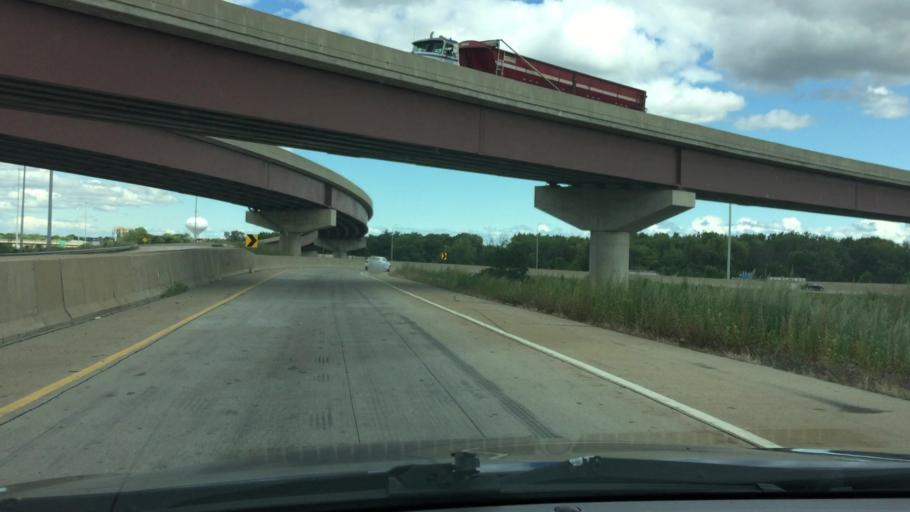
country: US
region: Illinois
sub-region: Cook County
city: Thornton
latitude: 41.5784
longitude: -87.5812
